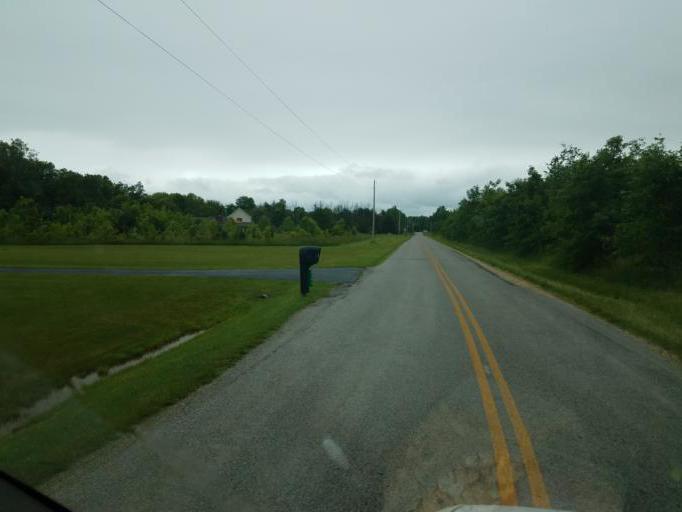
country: US
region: Ohio
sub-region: Morrow County
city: Cardington
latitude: 40.5226
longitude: -83.0126
